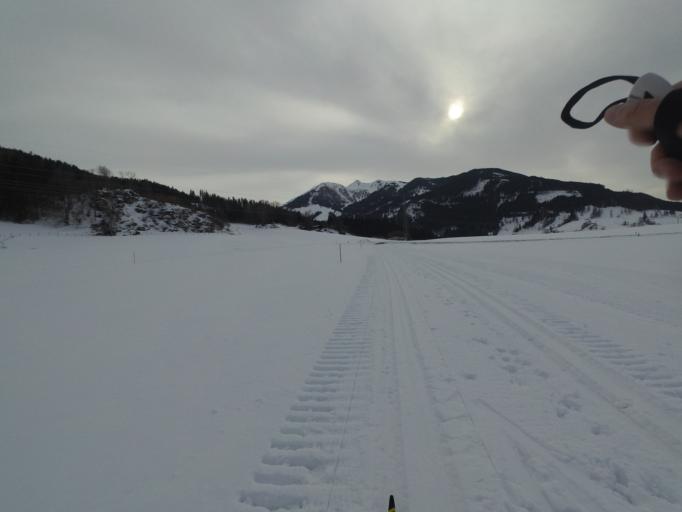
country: AT
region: Salzburg
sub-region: Politischer Bezirk Zell am See
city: Taxenbach
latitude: 47.2843
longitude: 12.9839
